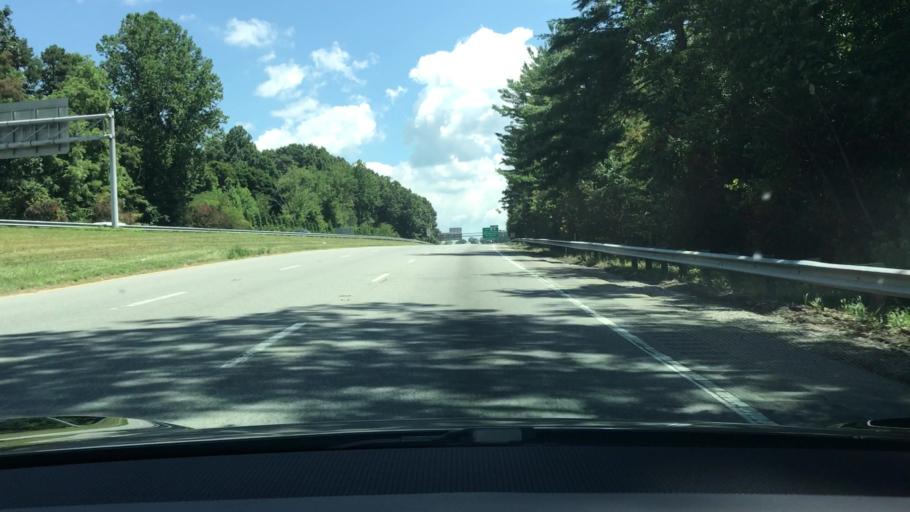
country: US
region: North Carolina
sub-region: Haywood County
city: Lake Junaluska
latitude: 35.5184
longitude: -82.9669
